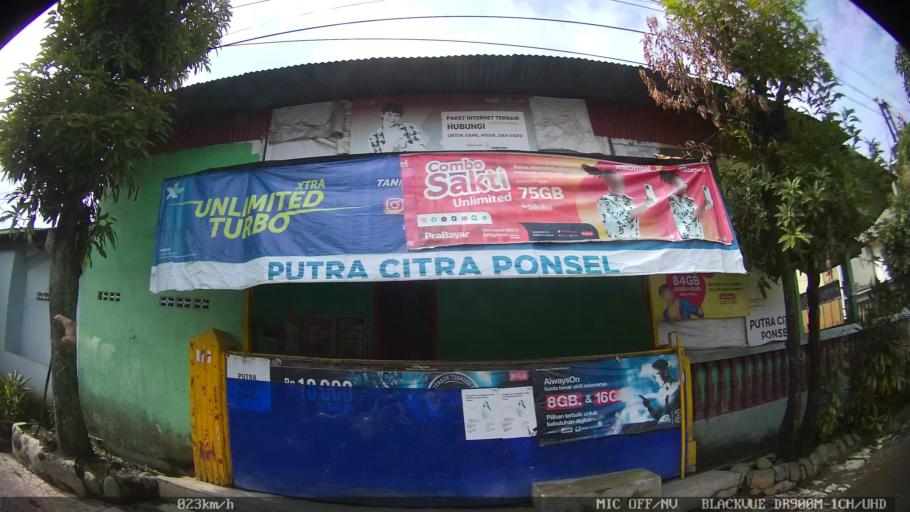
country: ID
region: North Sumatra
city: Medan
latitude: 3.6135
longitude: 98.6379
